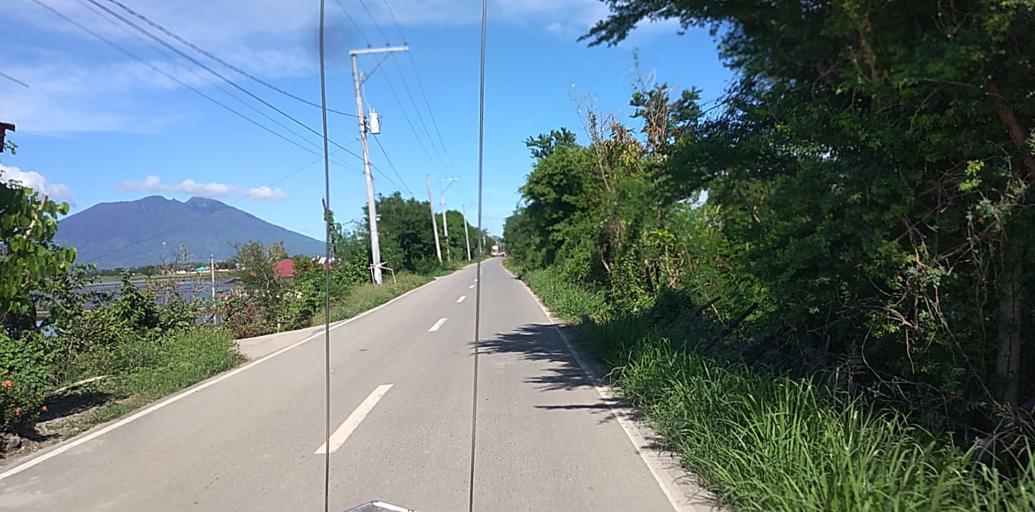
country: PH
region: Central Luzon
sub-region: Province of Pampanga
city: Candaba
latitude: 15.1160
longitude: 120.8148
